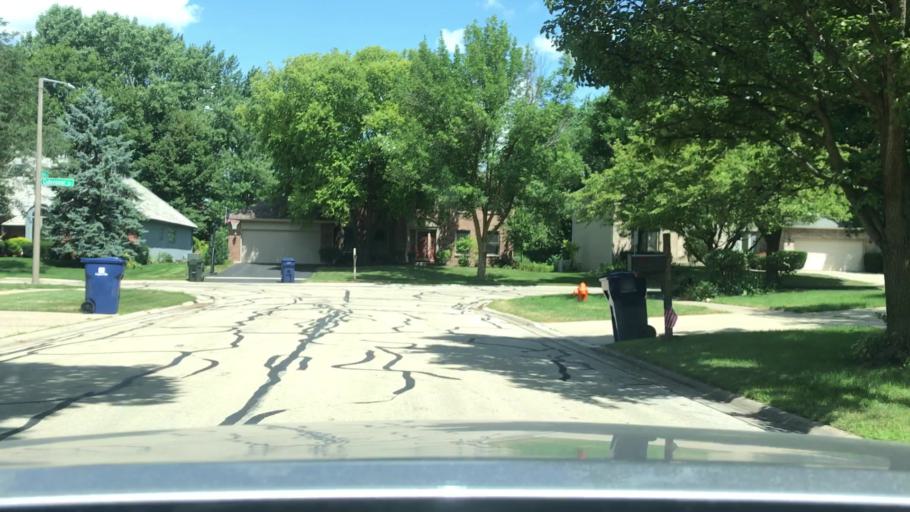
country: US
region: Illinois
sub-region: DuPage County
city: Naperville
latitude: 41.7591
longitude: -88.1049
